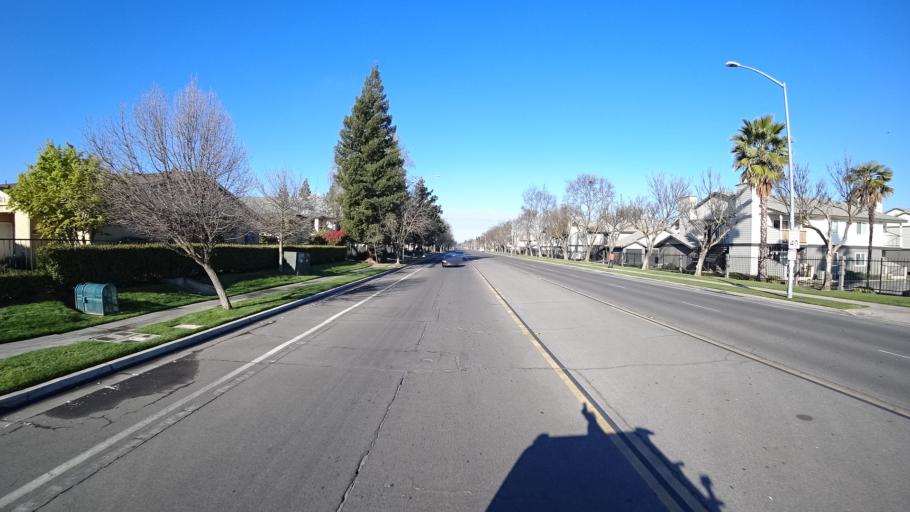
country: US
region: California
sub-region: Fresno County
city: Fresno
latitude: 36.8117
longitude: -119.8498
